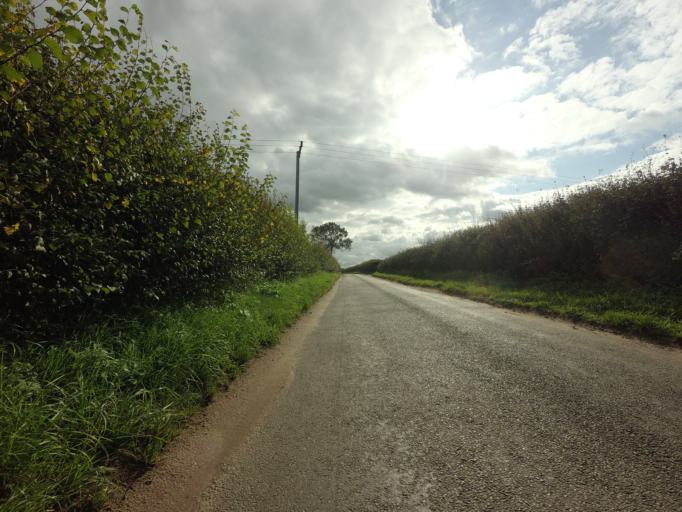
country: GB
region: England
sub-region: Norfolk
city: Snettisham
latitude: 52.8755
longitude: 0.5143
